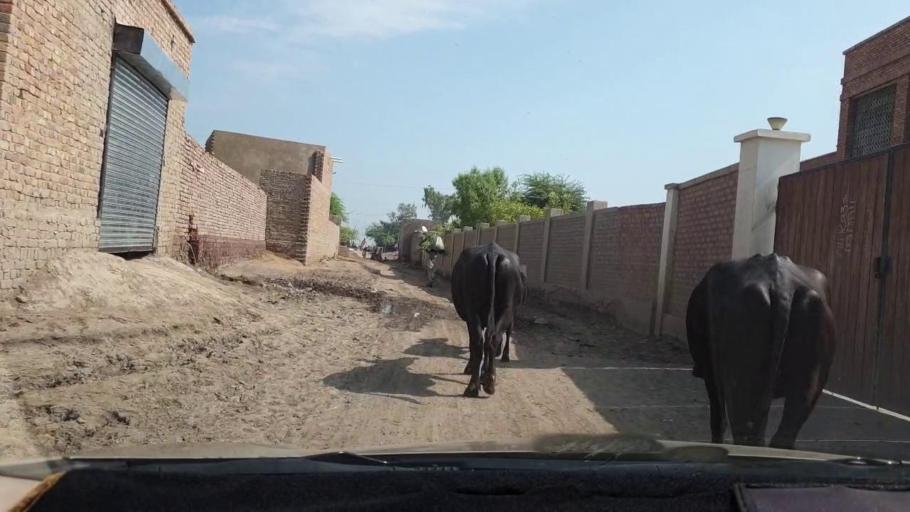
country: PK
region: Sindh
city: Larkana
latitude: 27.6659
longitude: 68.2227
